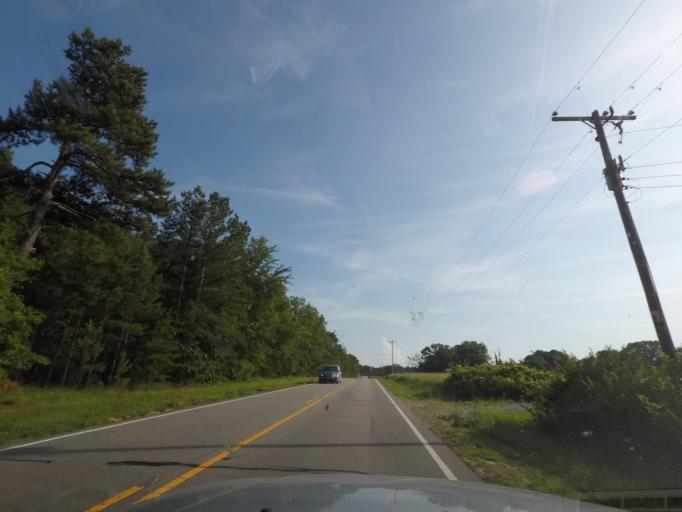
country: US
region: North Carolina
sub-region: Granville County
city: Oxford
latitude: 36.4188
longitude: -78.5872
